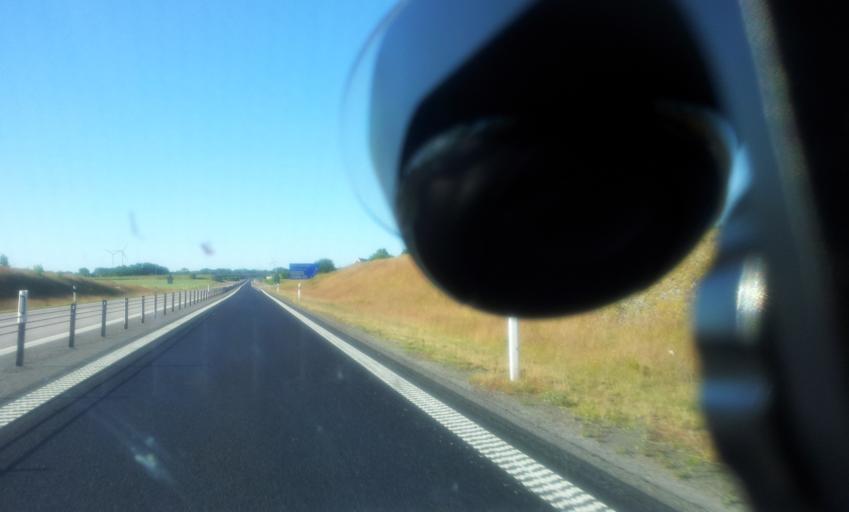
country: SE
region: Kalmar
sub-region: Torsas Kommun
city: Torsas
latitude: 56.4575
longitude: 16.0785
